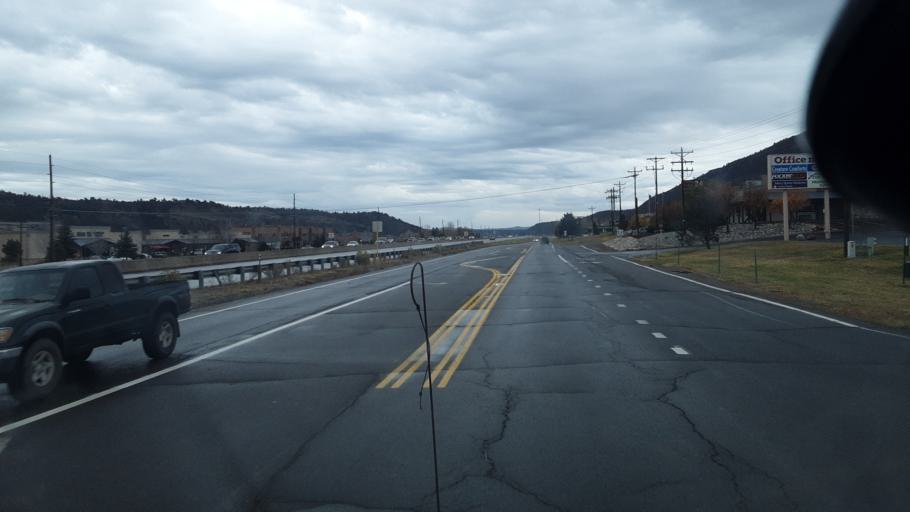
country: US
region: Colorado
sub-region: La Plata County
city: Durango
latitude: 37.2517
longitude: -107.8766
